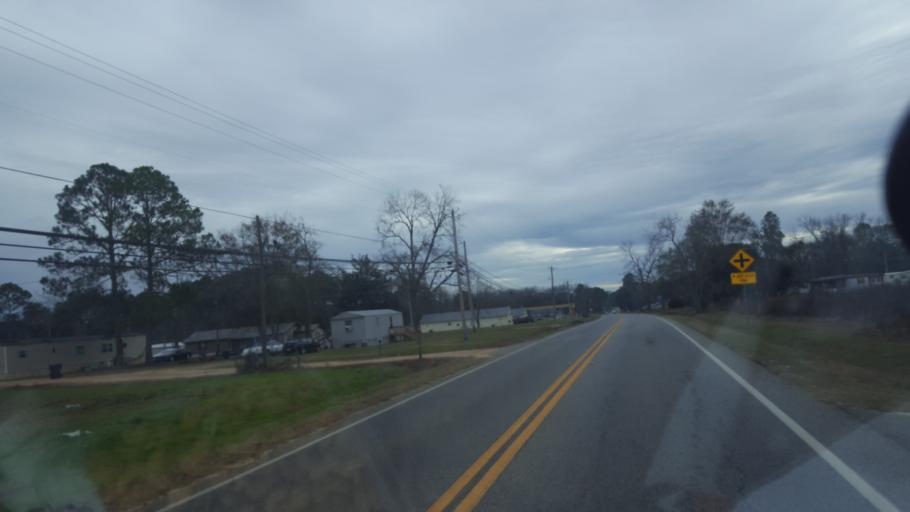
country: US
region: Georgia
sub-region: Ben Hill County
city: Fitzgerald
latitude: 31.7331
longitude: -83.2609
